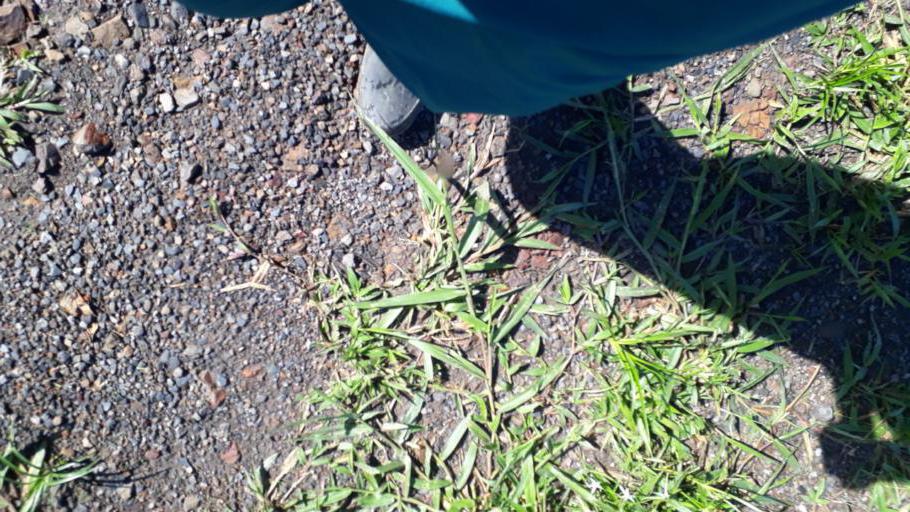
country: CO
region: Casanare
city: Nunchia
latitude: 5.6628
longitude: -72.4227
